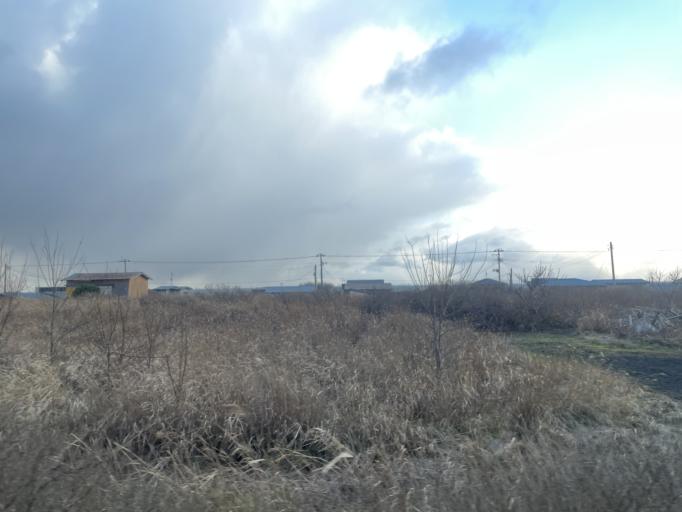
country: JP
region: Aomori
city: Mutsu
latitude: 41.0918
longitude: 141.2496
